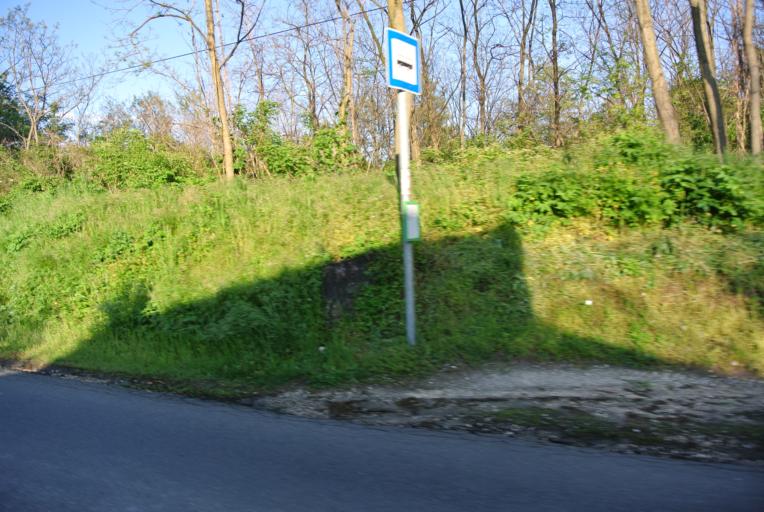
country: HU
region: Komarom-Esztergom
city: Dorog
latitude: 47.7018
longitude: 18.7349
